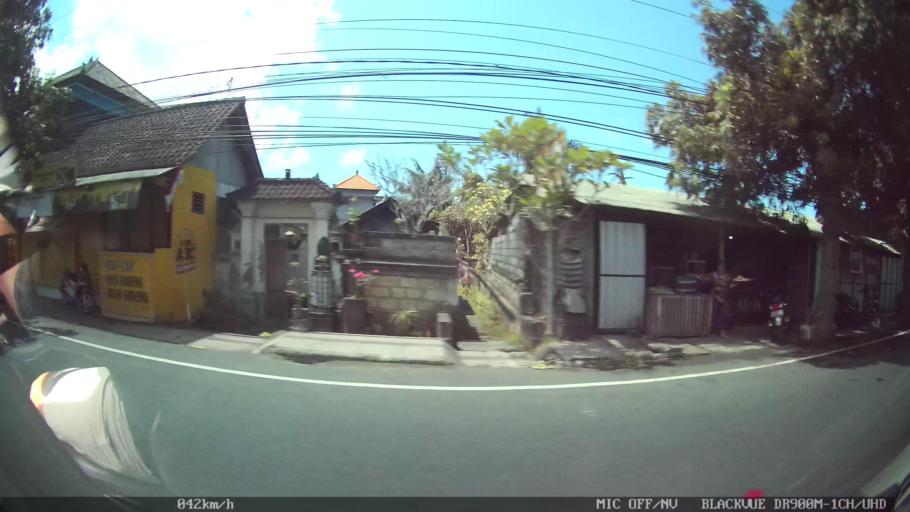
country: ID
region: Bali
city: Banjar Pasekan
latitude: -8.5912
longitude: 115.2825
